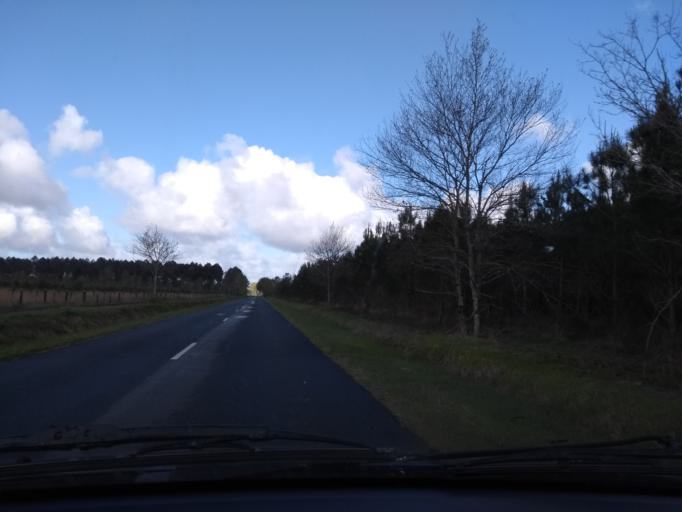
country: FR
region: Aquitaine
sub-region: Departement de la Gironde
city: Mios
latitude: 44.5501
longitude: -0.9748
